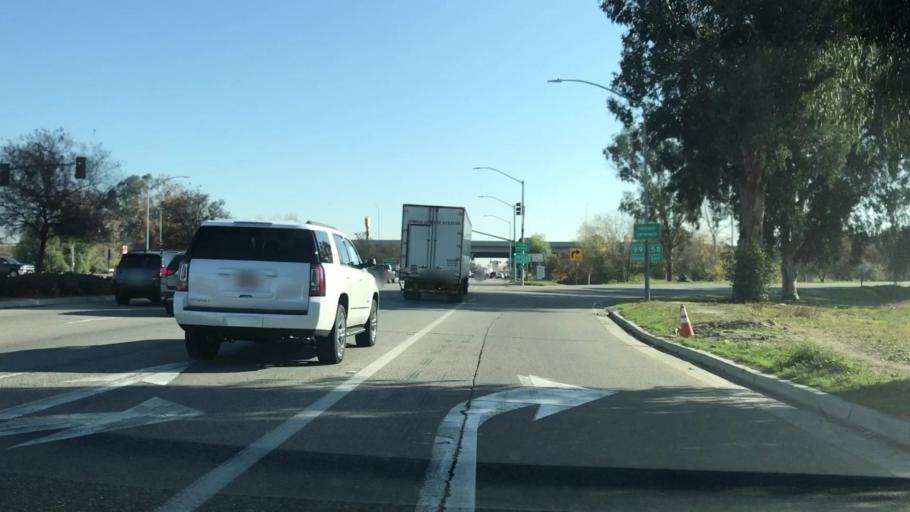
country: US
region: California
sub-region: Kern County
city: Bakersfield
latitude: 35.3831
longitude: -119.0467
